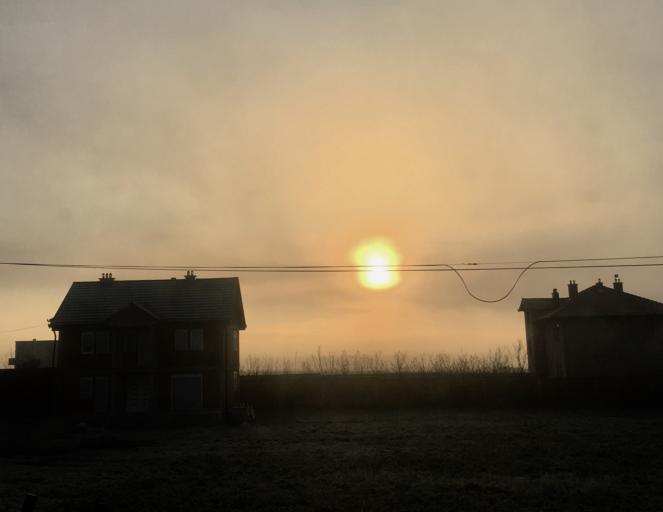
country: XK
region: Pristina
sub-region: Komuna e Drenasit
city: Glogovac
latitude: 42.6042
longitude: 20.9023
